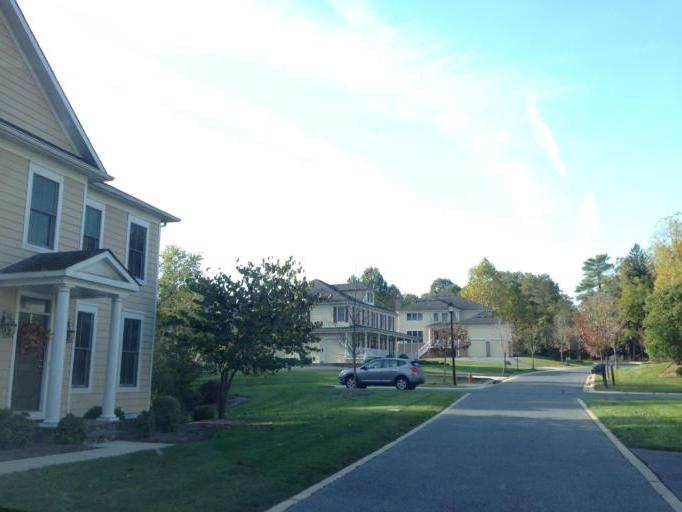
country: US
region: Maryland
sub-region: Howard County
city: Ellicott City
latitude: 39.2760
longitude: -76.7984
